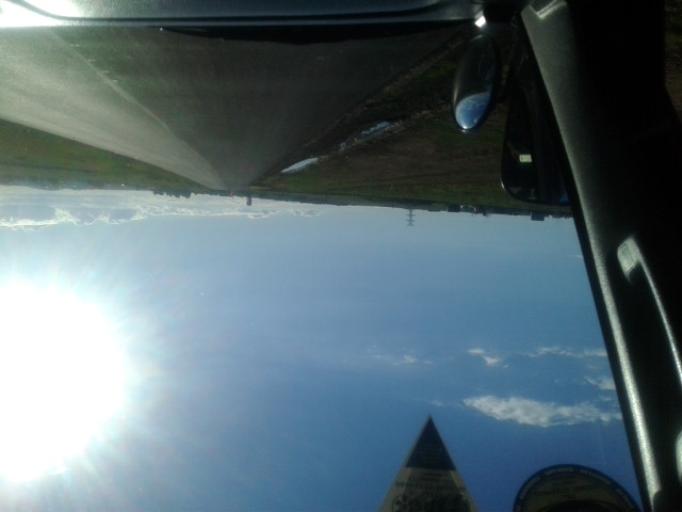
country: LS
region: Maseru
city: Maseru
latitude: -29.3097
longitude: 27.6005
